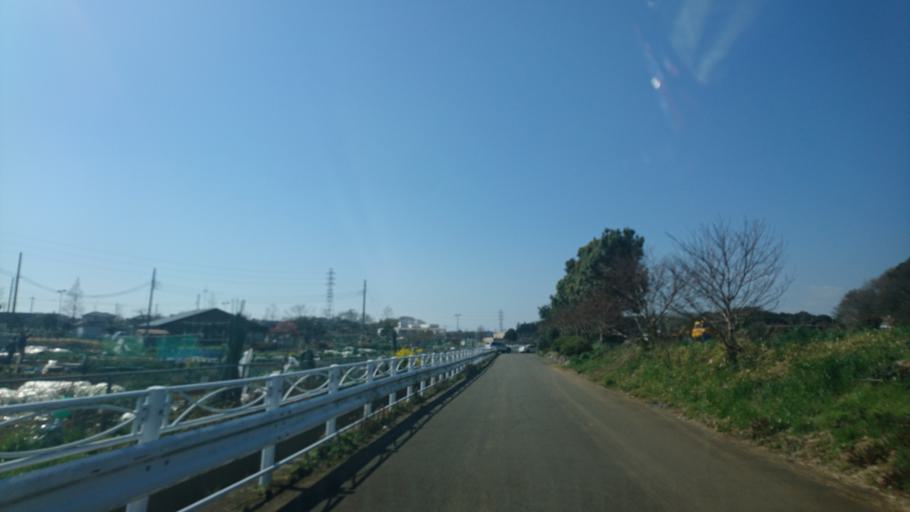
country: JP
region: Kanagawa
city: Fujisawa
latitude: 35.3911
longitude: 139.4354
